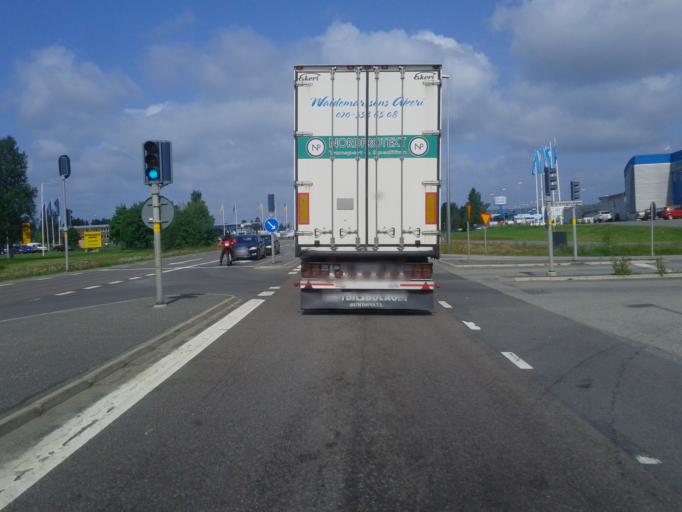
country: SE
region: Vaesterbotten
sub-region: Skelleftea Kommun
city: Skelleftea
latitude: 64.7354
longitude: 20.9680
